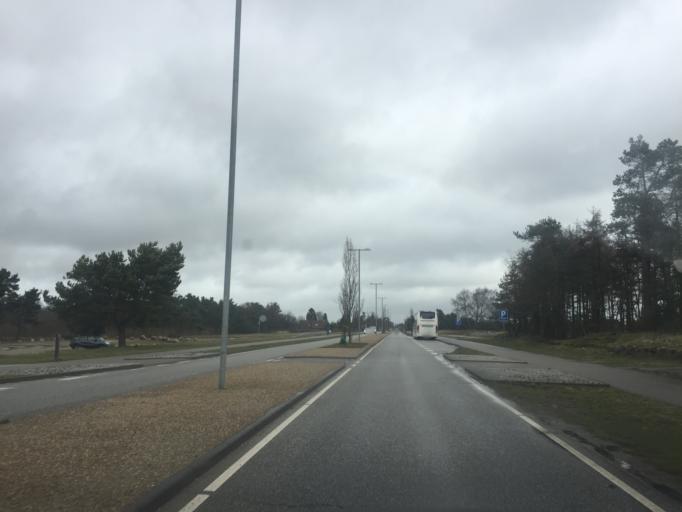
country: DK
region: Zealand
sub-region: Solrod Kommune
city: Solrod Strand
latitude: 55.5510
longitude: 12.2443
